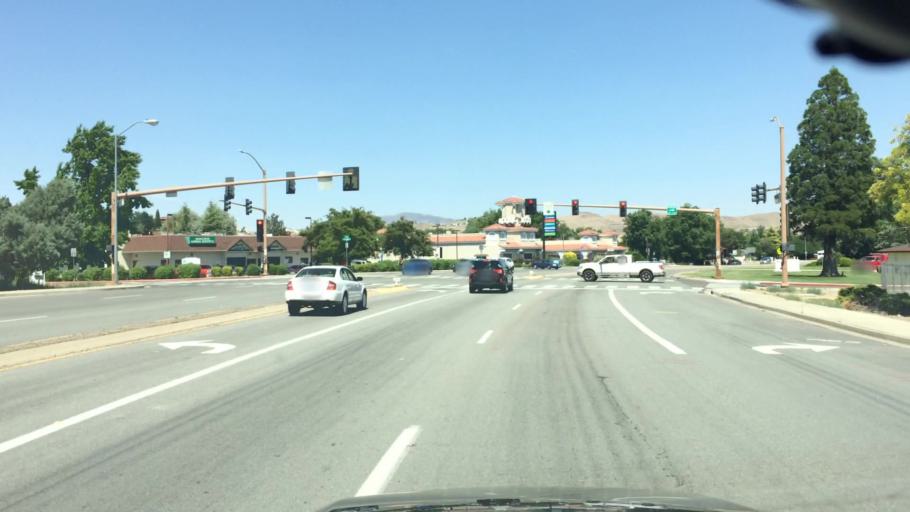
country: US
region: Nevada
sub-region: Washoe County
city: Sparks
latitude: 39.5559
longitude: -119.7342
